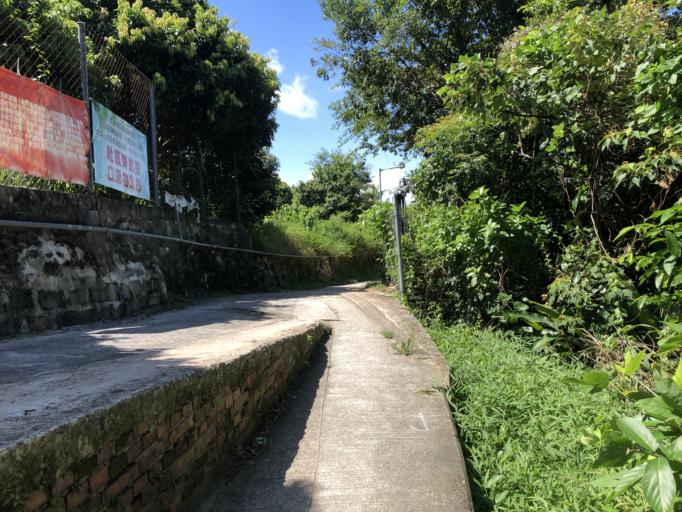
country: HK
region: Tuen Mun
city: Tuen Mun
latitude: 22.2894
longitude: 113.9788
